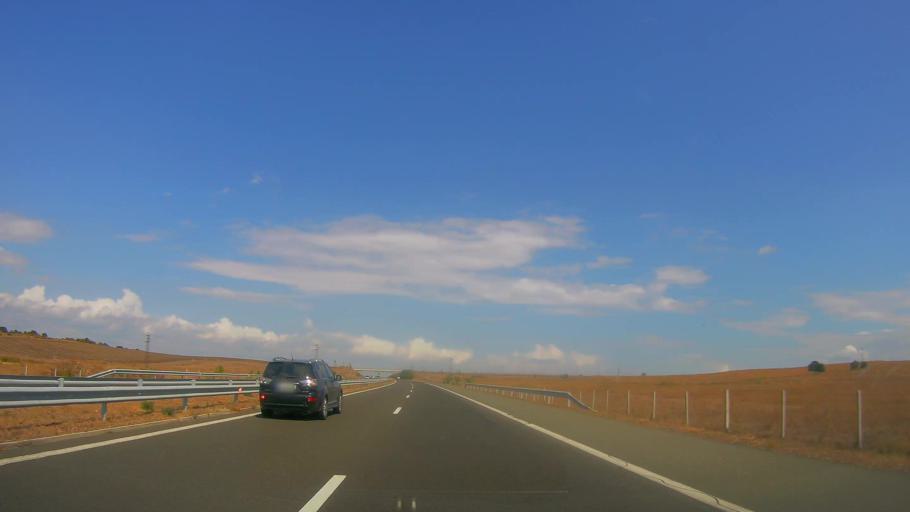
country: BG
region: Burgas
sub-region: Obshtina Karnobat
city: Karnobat
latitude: 42.5650
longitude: 26.8653
